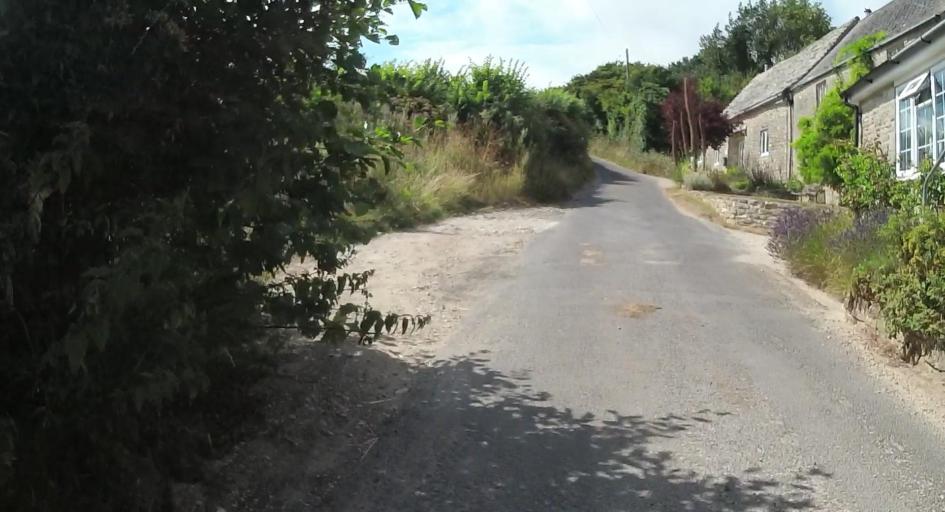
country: GB
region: England
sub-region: Dorset
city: Swanage
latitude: 50.6304
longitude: -2.0100
